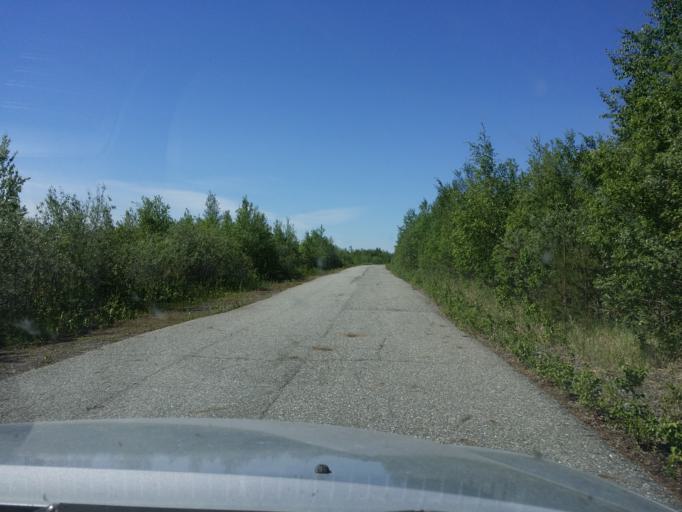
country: RU
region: Khanty-Mansiyskiy Avtonomnyy Okrug
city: Surgut
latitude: 61.4169
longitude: 73.8355
